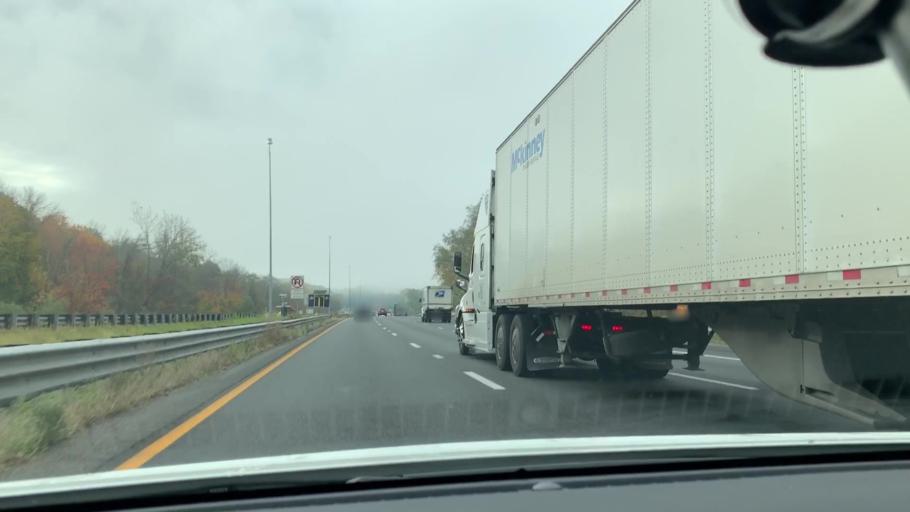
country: US
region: Massachusetts
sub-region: Hampden County
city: Longmeadow
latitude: 42.0359
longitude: -72.5890
